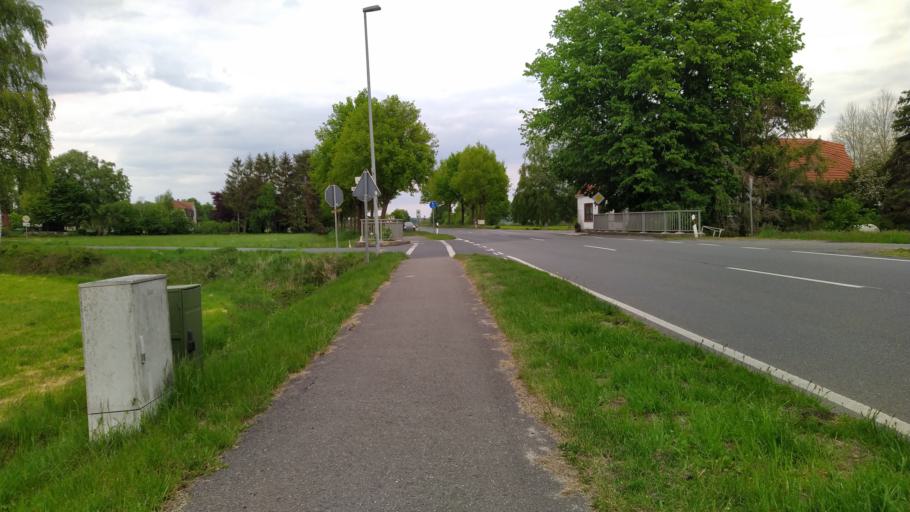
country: DE
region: Lower Saxony
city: Grasberg
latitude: 53.2008
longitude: 9.0284
